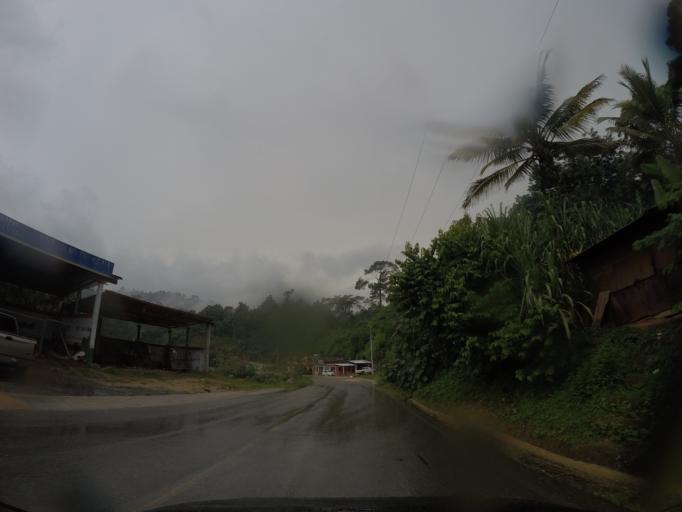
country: MX
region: Oaxaca
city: San Gabriel Mixtepec
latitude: 16.0888
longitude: -97.0799
